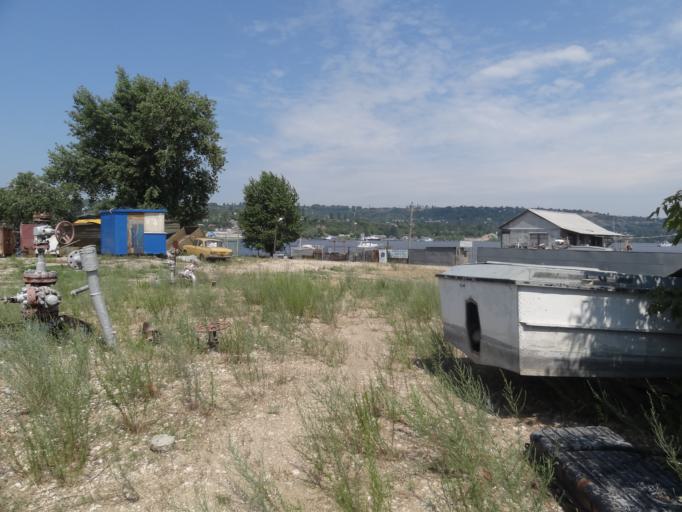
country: RU
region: Saratov
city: Engel's
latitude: 51.5384
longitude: 46.0864
